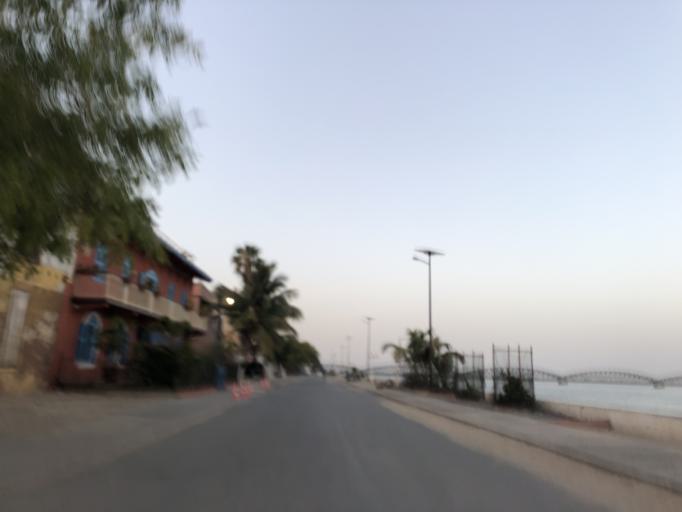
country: SN
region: Saint-Louis
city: Saint-Louis
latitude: 16.0224
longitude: -16.5041
